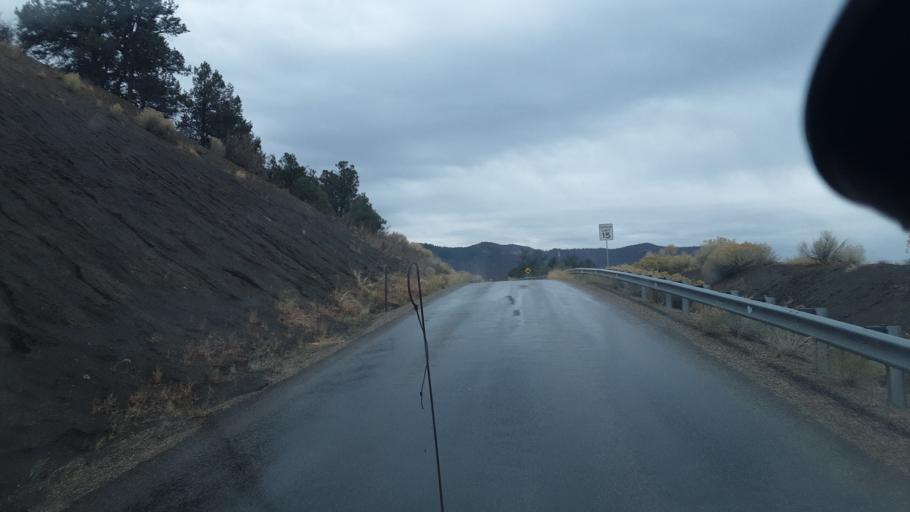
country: US
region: Colorado
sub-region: La Plata County
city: Durango
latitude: 37.2370
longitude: -107.9069
